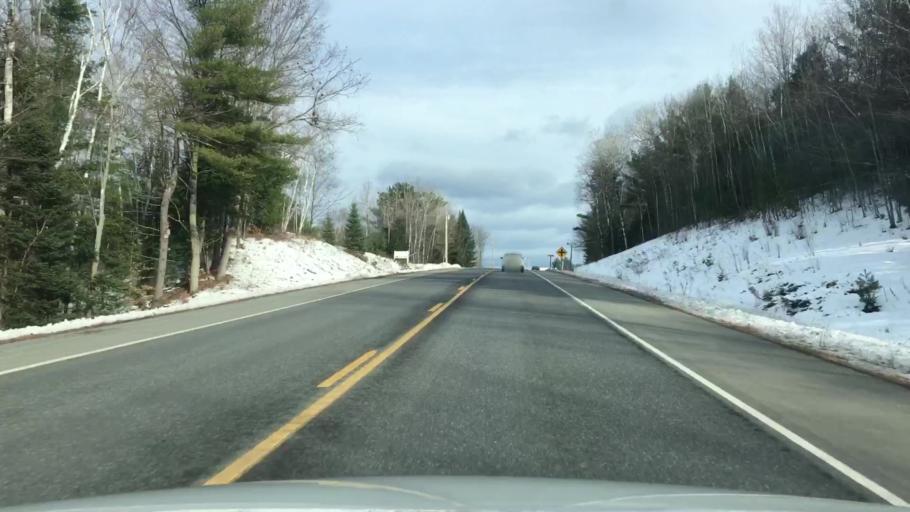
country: US
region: Maine
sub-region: Kennebec County
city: Monmouth
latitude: 44.2663
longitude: -70.0371
